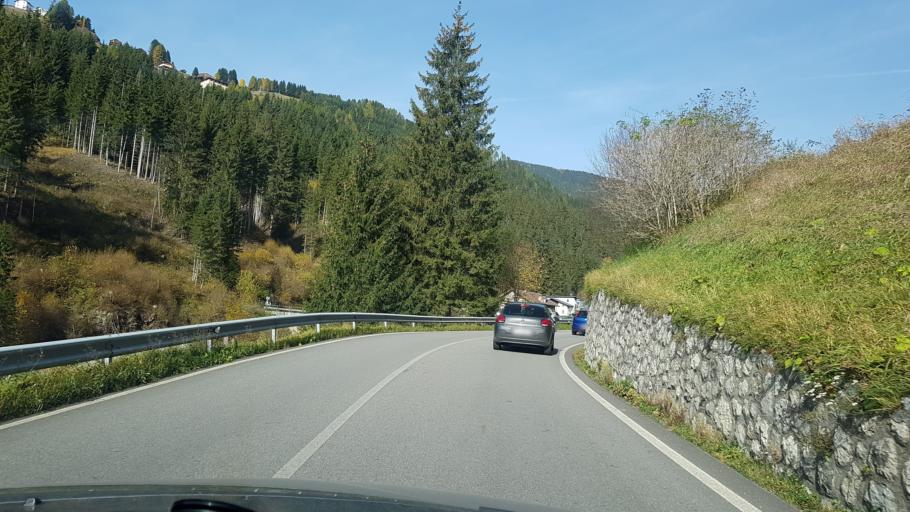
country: IT
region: Veneto
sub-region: Provincia di Belluno
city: San Nicolo Comelico
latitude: 46.5876
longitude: 12.5237
